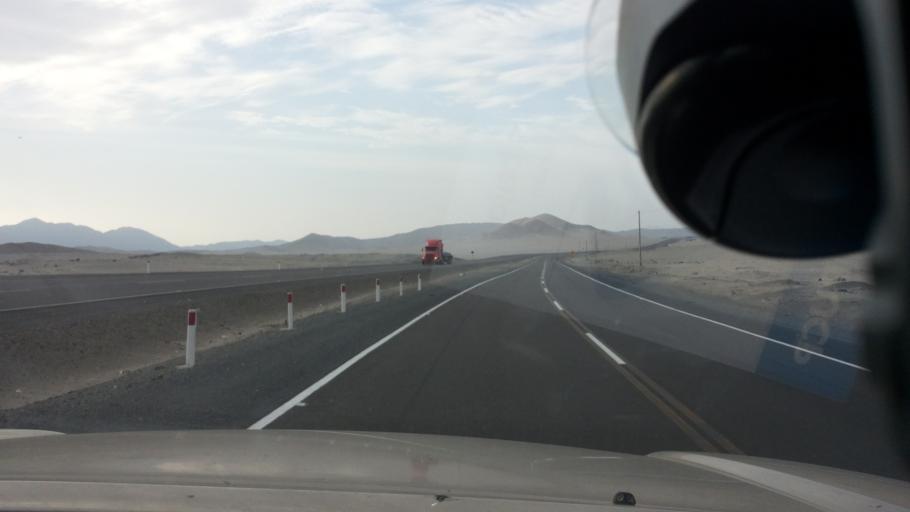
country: PE
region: Ancash
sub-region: Provincia de Casma
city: Casma
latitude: -9.5540
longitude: -78.2669
